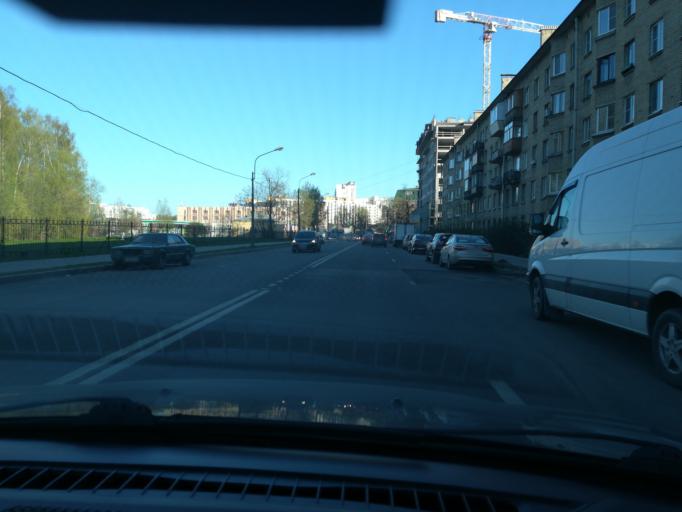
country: RU
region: St.-Petersburg
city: Vasyl'evsky Ostrov
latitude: 59.9401
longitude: 30.2430
